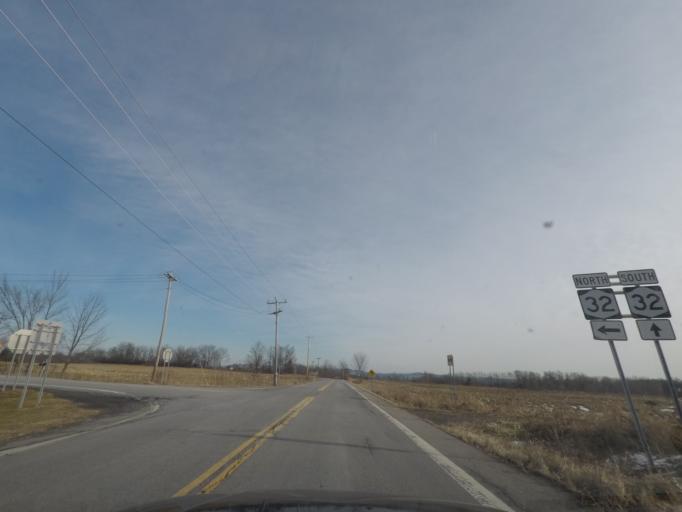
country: US
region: New York
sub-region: Saratoga County
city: Stillwater
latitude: 42.9846
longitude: -73.6675
